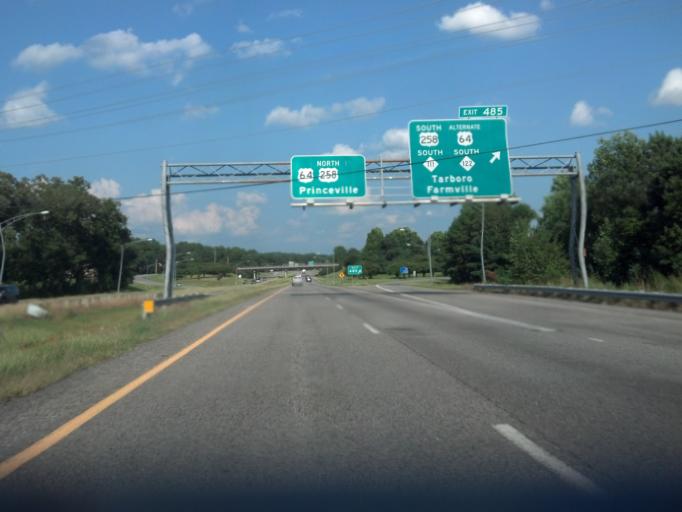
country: US
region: North Carolina
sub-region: Edgecombe County
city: Tarboro
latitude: 35.8853
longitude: -77.5526
